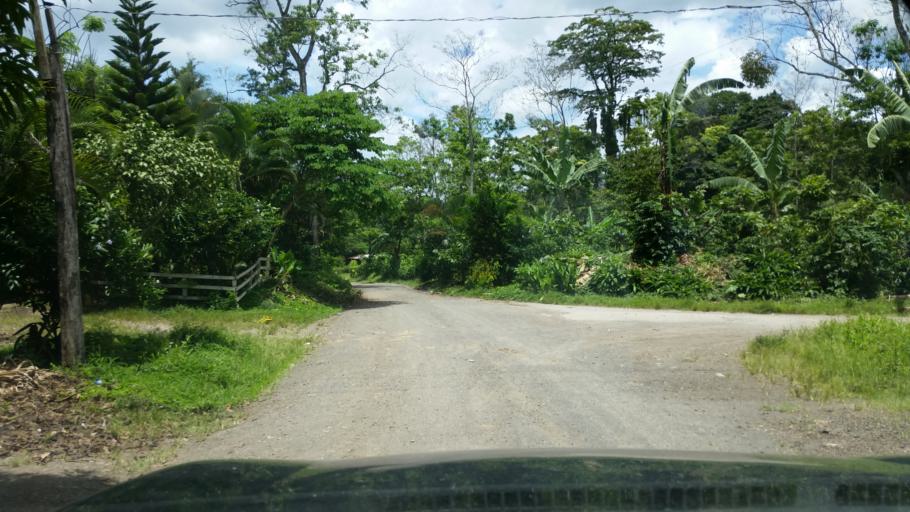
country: NI
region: Atlantico Norte (RAAN)
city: Waslala
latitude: 13.2579
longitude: -85.6203
